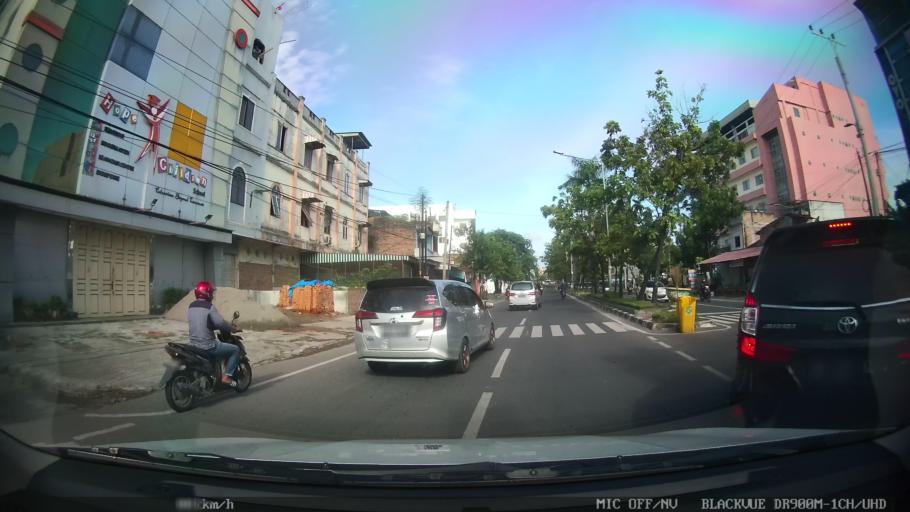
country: ID
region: North Sumatra
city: Medan
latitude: 3.6074
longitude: 98.6593
